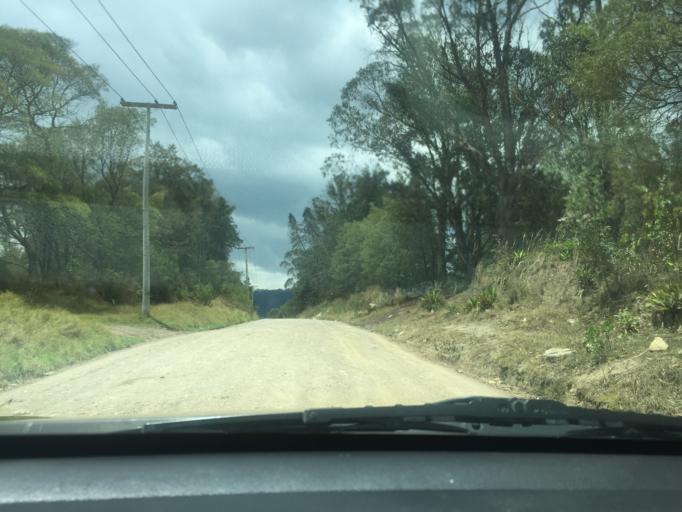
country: CO
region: Cundinamarca
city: Facatativa
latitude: 4.8074
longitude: -74.3116
